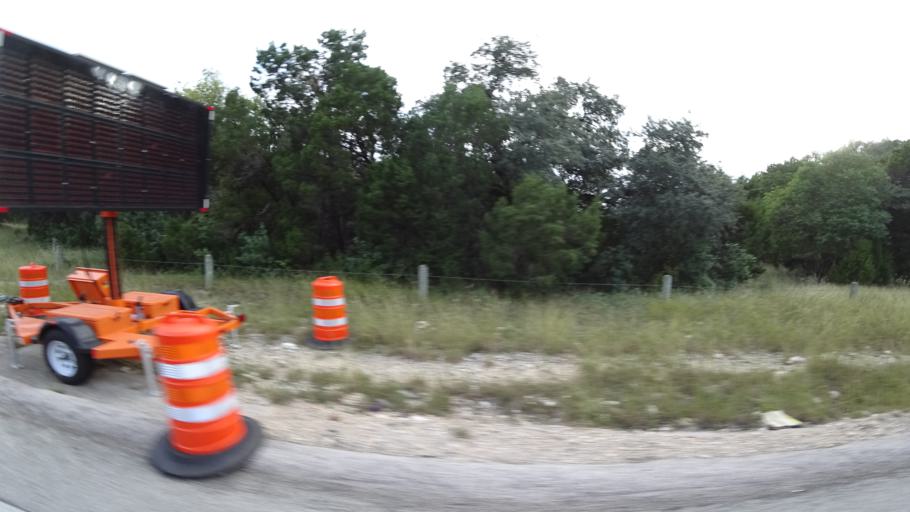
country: US
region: Texas
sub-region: Travis County
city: West Lake Hills
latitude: 30.2904
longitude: -97.7920
